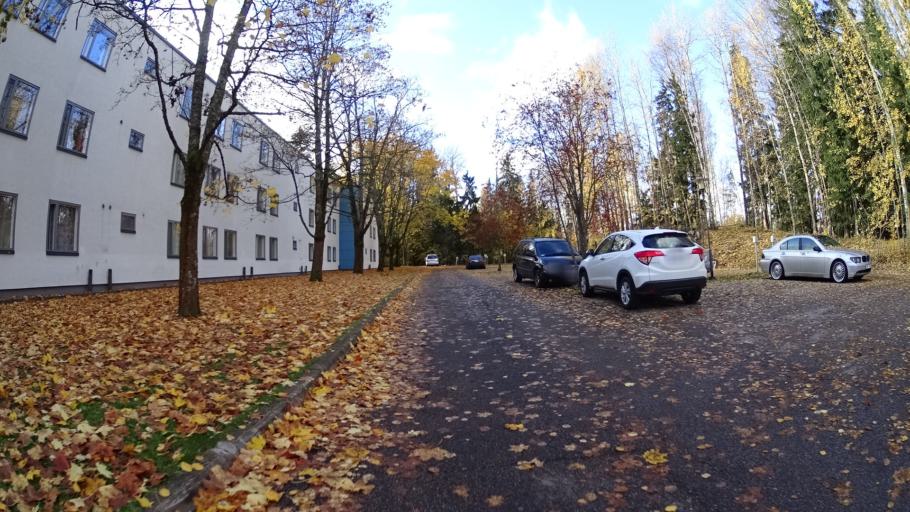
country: FI
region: Uusimaa
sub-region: Helsinki
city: Kilo
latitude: 60.2817
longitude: 24.8388
